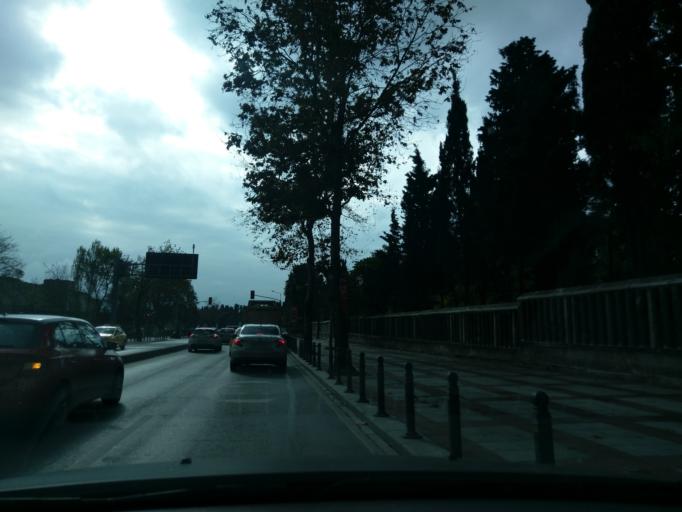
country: TR
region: Istanbul
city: Zeytinburnu
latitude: 41.0150
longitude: 28.9214
